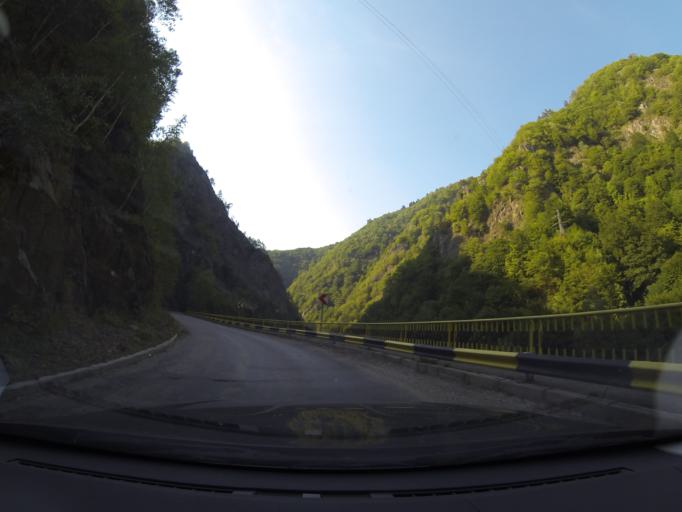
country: RO
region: Arges
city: Poenari
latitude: 45.3529
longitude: 24.6381
